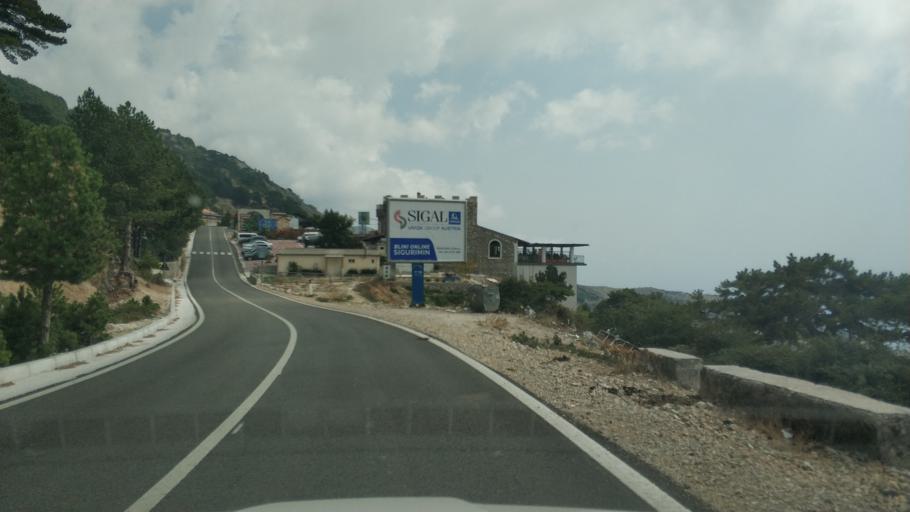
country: AL
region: Vlore
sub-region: Rrethi i Vlores
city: Vranisht
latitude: 40.1973
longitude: 19.5938
